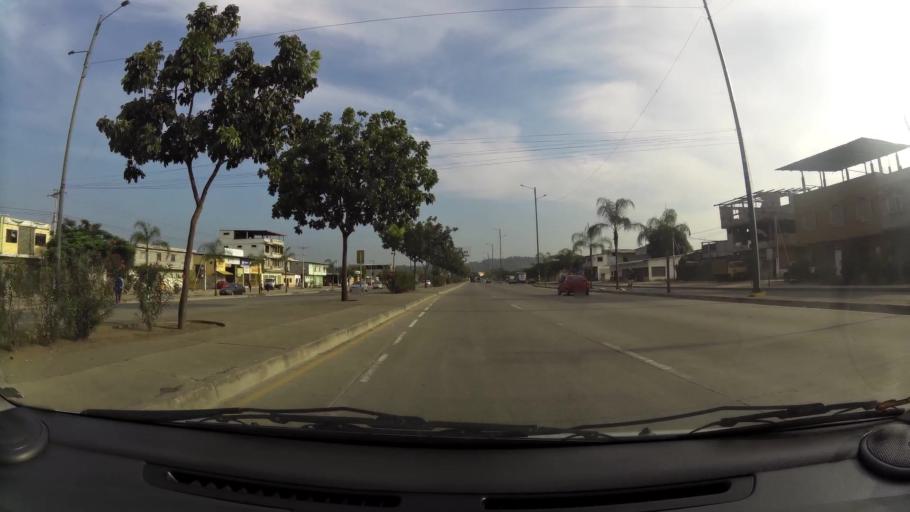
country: EC
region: Guayas
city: Eloy Alfaro
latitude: -2.0898
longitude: -79.8951
